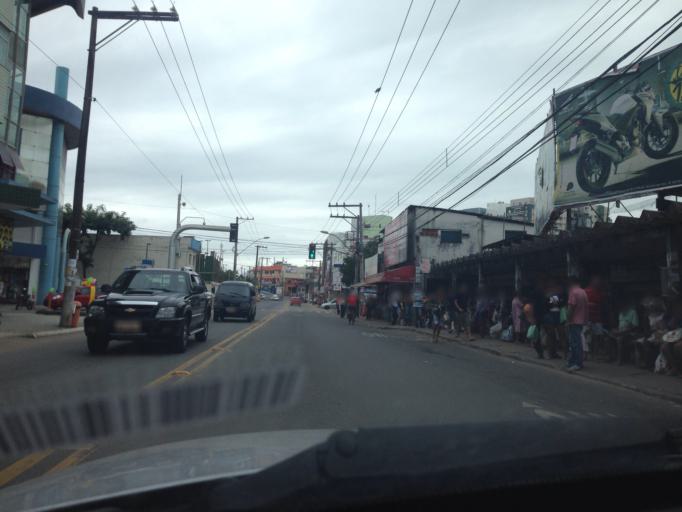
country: BR
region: Espirito Santo
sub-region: Guarapari
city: Guarapari
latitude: -20.6709
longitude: -40.5000
